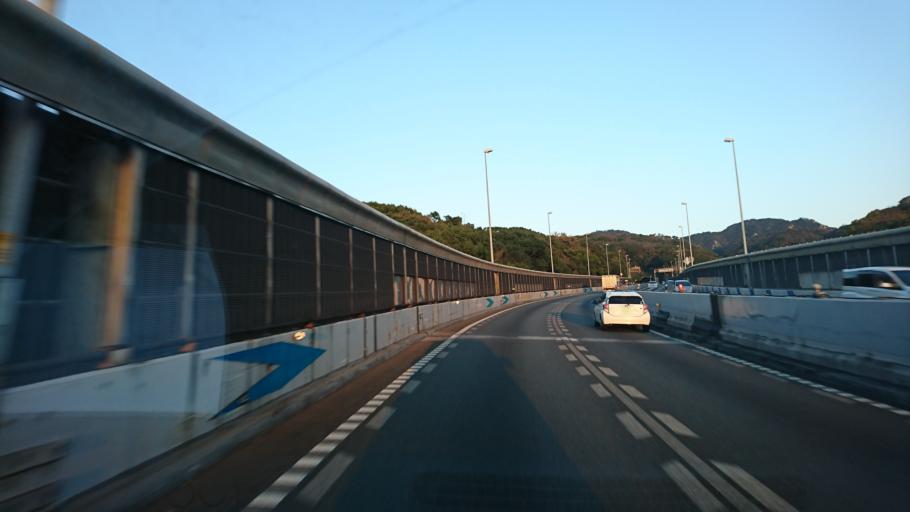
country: JP
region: Hyogo
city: Kobe
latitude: 34.6527
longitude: 135.1201
